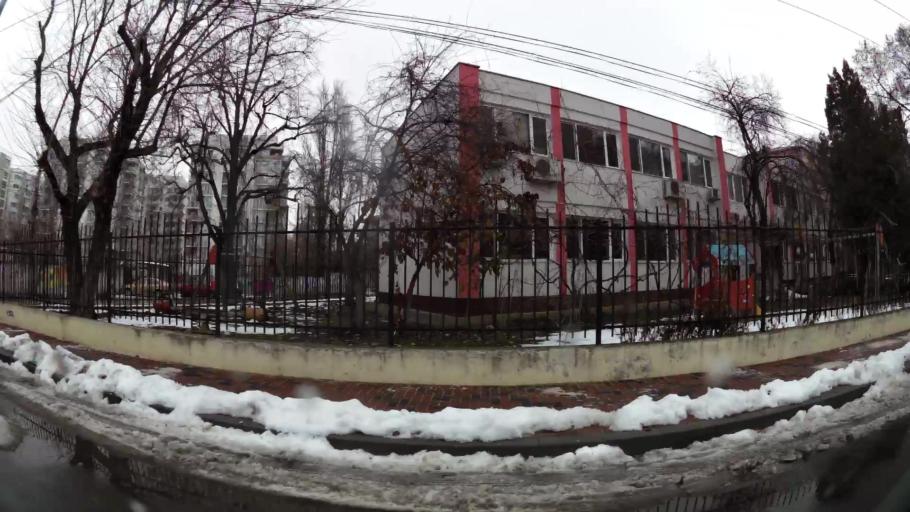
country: RO
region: Ilfov
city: Dobroesti
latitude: 44.4186
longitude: 26.1716
